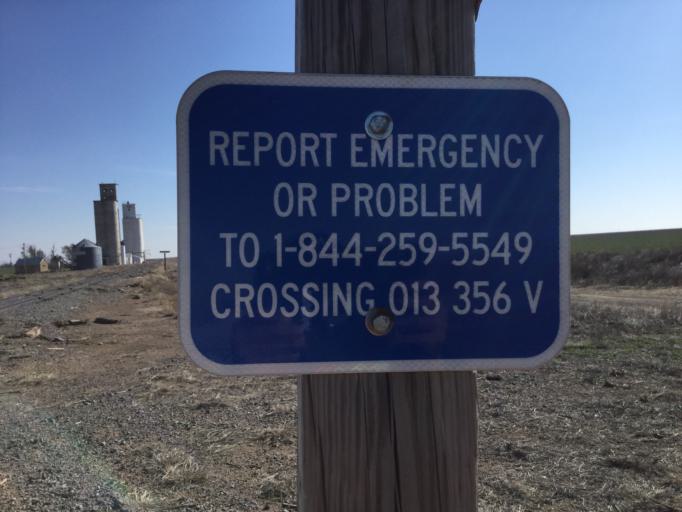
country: US
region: Kansas
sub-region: Stanton County
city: Johnson
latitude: 37.4696
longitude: -102.0417
